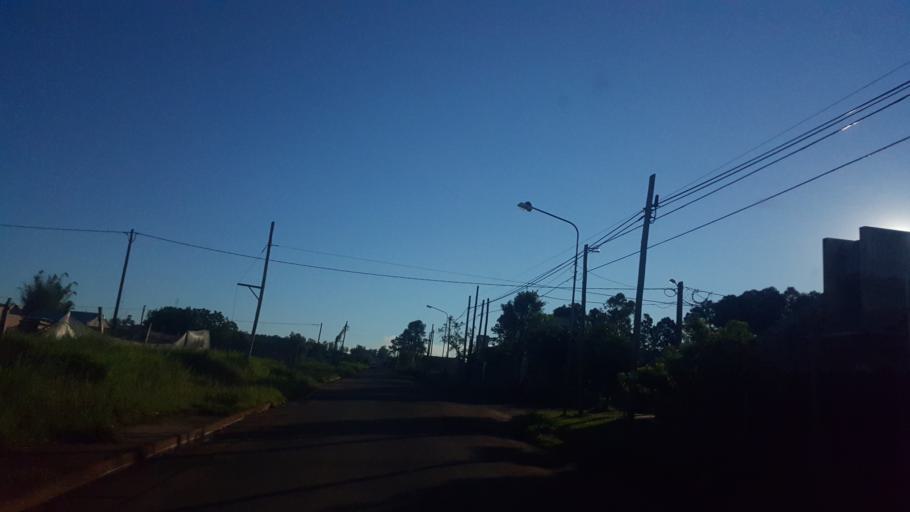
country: AR
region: Misiones
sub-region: Departamento de Capital
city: Posadas
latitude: -27.4271
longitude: -55.9431
